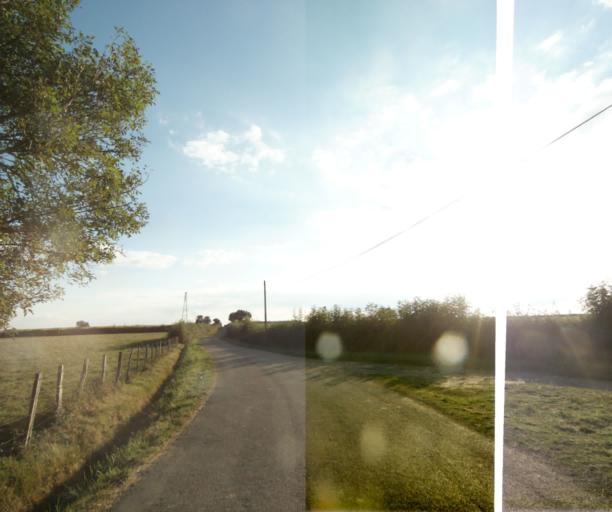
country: FR
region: Bourgogne
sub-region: Departement de Saone-et-Loire
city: Perrecy-les-Forges
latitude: 46.5855
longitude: 4.1679
